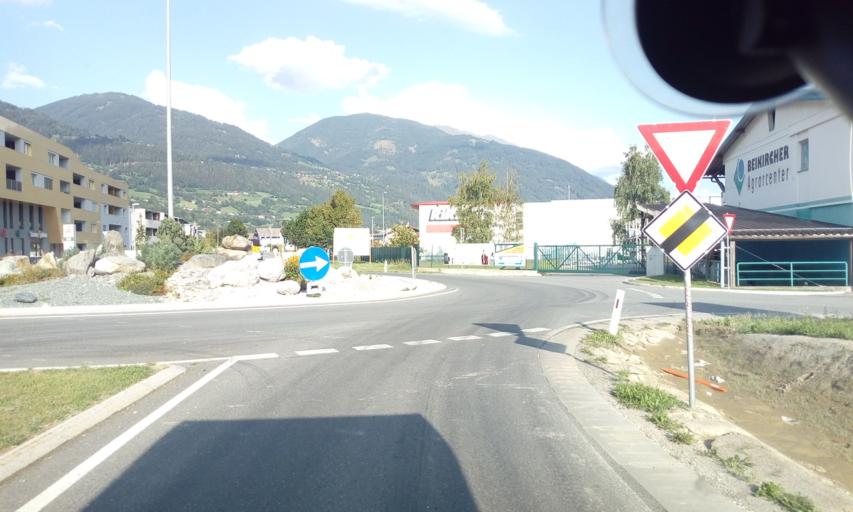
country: AT
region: Tyrol
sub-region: Politischer Bezirk Lienz
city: Tristach
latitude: 46.8299
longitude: 12.8036
